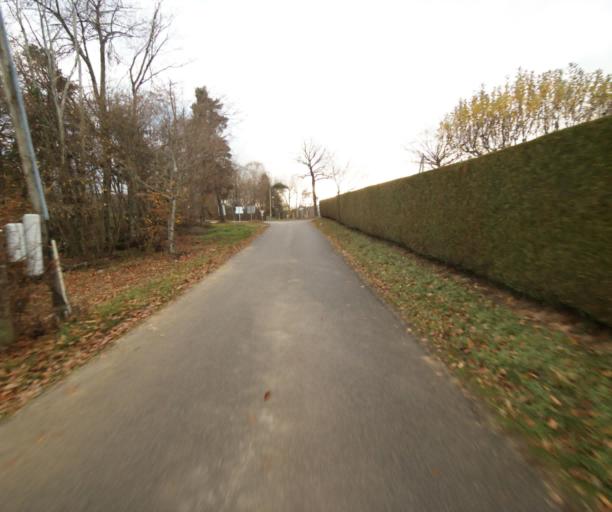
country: FR
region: Limousin
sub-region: Departement de la Correze
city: Sainte-Fortunade
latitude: 45.2126
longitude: 1.7802
